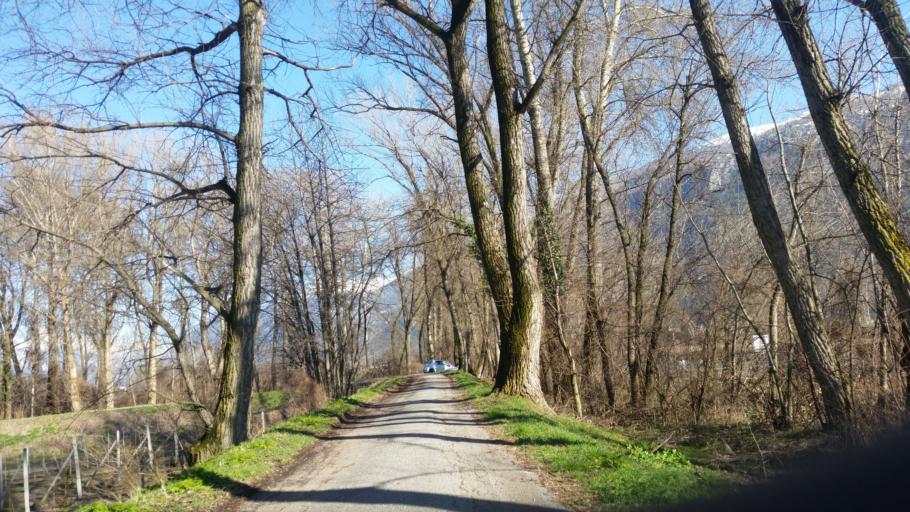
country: CH
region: Valais
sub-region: Sion District
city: Saint-Leonard
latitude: 46.2452
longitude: 7.3974
